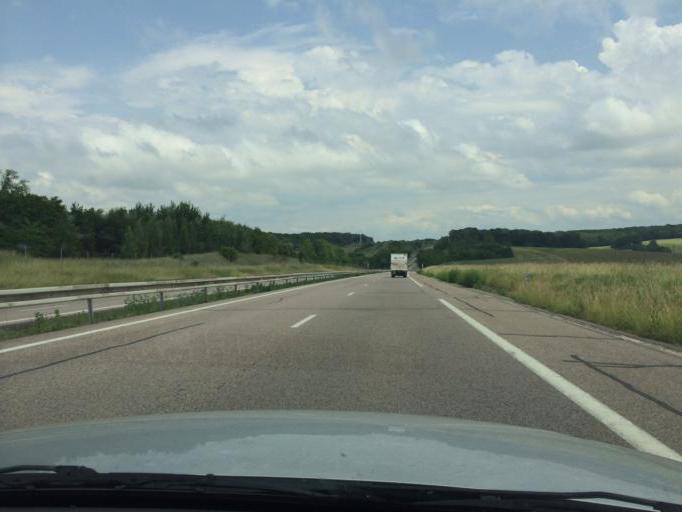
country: FR
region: Champagne-Ardenne
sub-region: Departement de la Marne
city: Dormans
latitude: 49.1441
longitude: 3.6337
